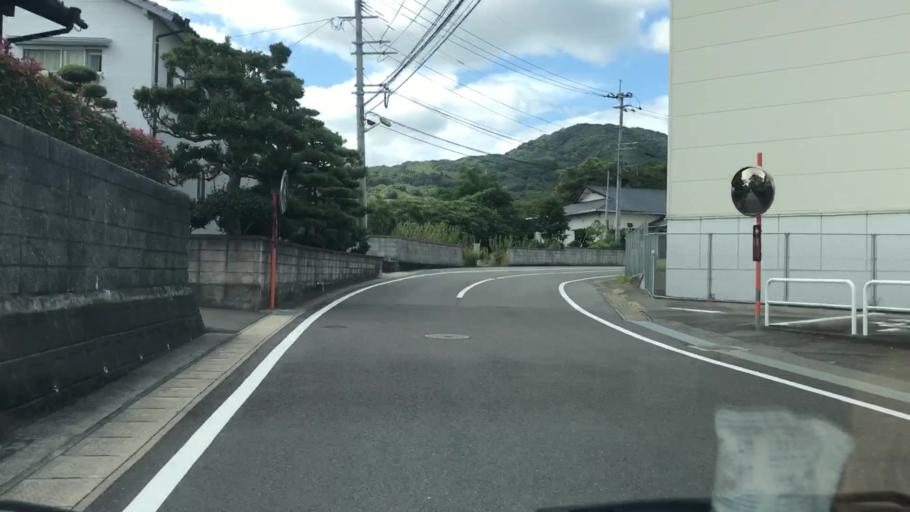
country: JP
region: Saga Prefecture
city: Takeocho-takeo
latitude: 33.2296
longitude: 130.1414
